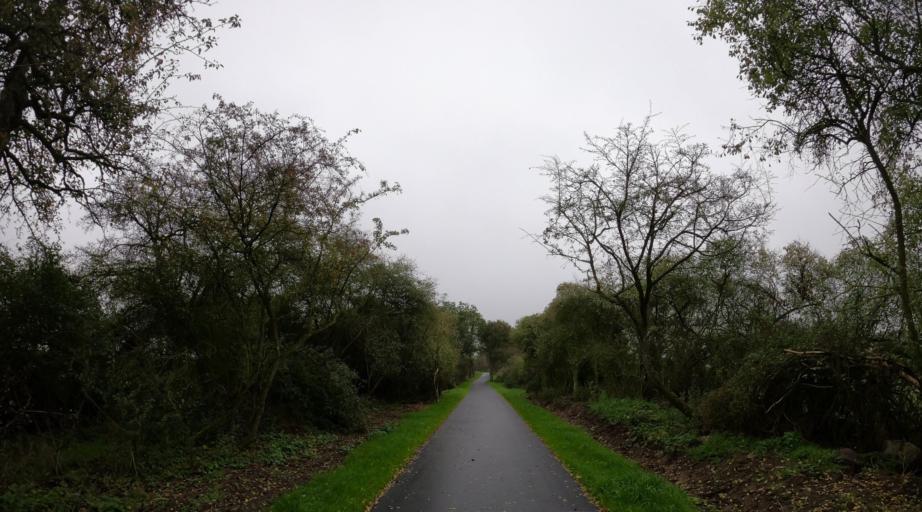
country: PL
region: West Pomeranian Voivodeship
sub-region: Powiat mysliborski
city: Mysliborz
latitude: 52.9128
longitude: 14.7458
